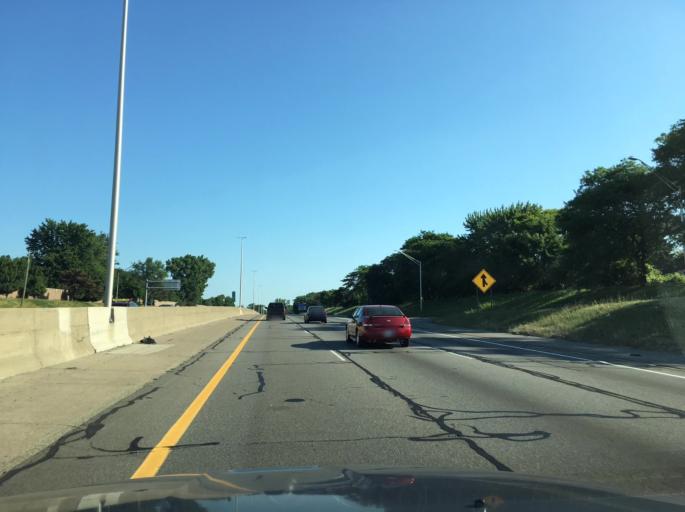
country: US
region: Michigan
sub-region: Macomb County
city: Roseville
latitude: 42.4788
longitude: -82.9166
